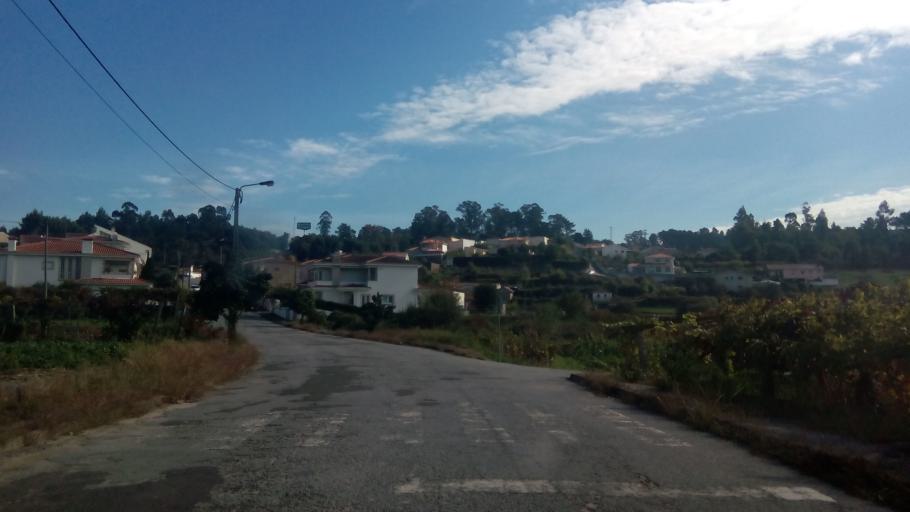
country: PT
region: Porto
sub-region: Paredes
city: Casteloes de Cepeda
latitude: 41.1967
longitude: -8.3320
